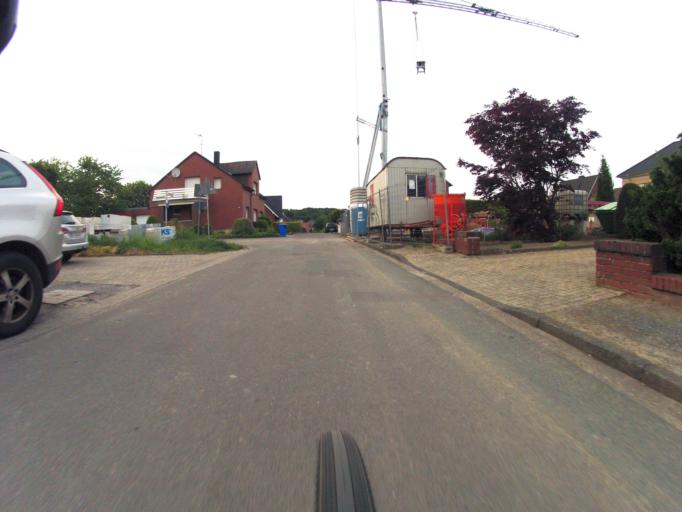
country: DE
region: North Rhine-Westphalia
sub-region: Regierungsbezirk Munster
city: Mettingen
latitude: 52.2684
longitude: 7.7727
